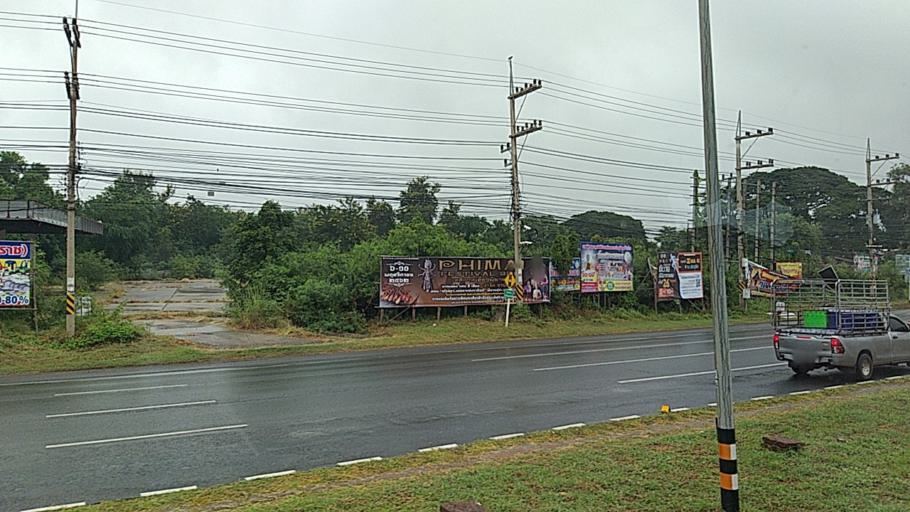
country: TH
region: Nakhon Ratchasima
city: Phimai
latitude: 15.2547
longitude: 102.4130
